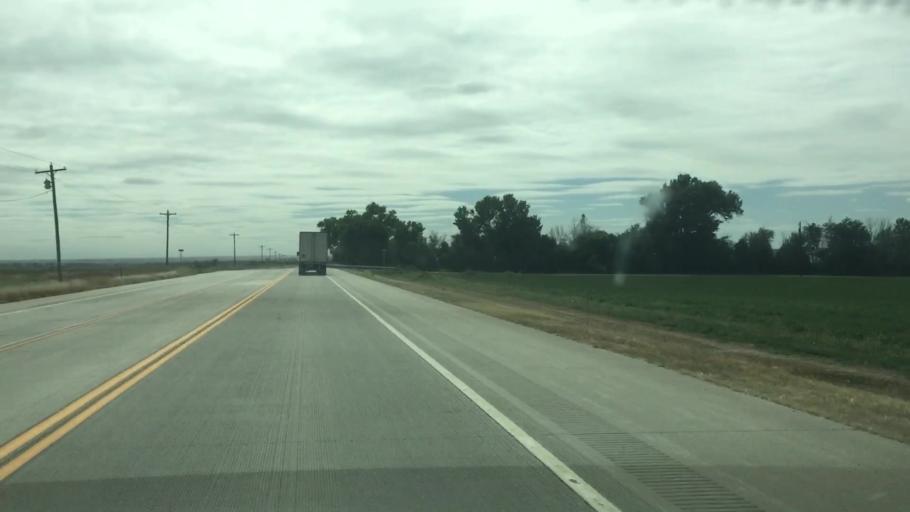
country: US
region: Colorado
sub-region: Prowers County
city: Lamar
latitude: 38.2029
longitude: -102.7242
